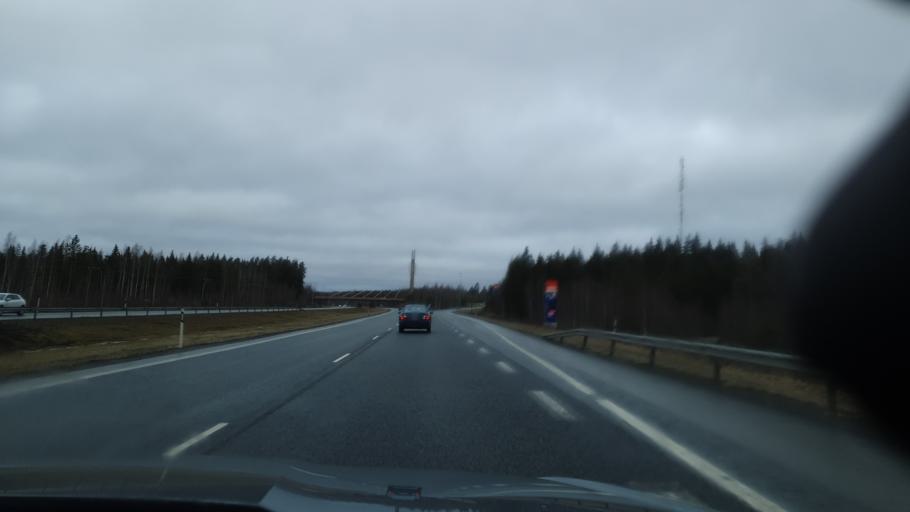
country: FI
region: Pirkanmaa
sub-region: Etelae-Pirkanmaa
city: Viiala
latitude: 61.2504
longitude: 23.8382
